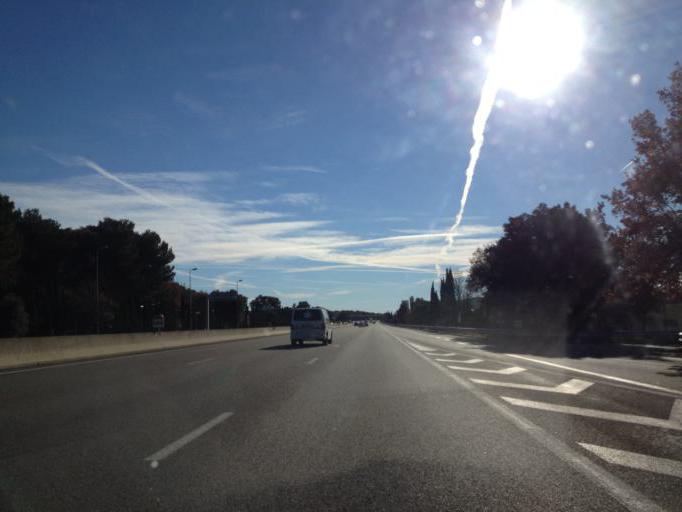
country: FR
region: Provence-Alpes-Cote d'Azur
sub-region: Departement du Vaucluse
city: Sorgues
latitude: 44.0206
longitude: 4.8890
